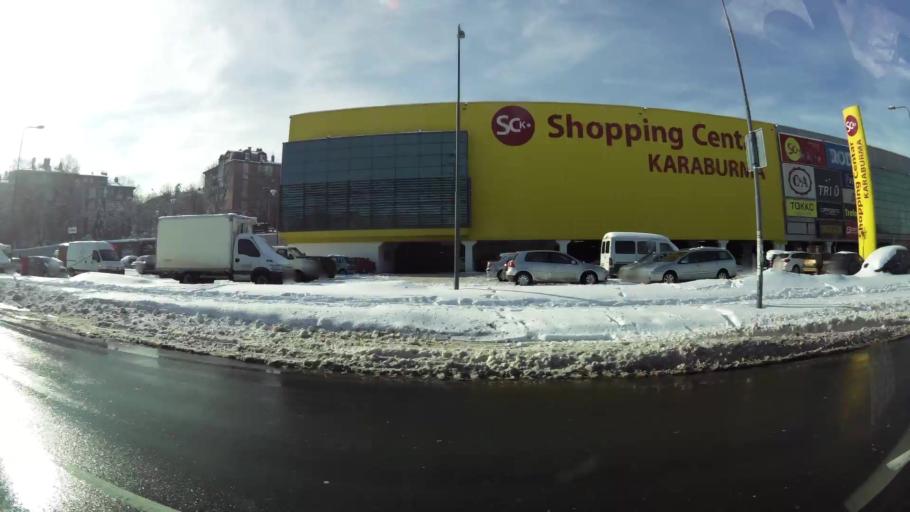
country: RS
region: Central Serbia
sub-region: Belgrade
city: Palilula
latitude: 44.8112
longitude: 20.5231
